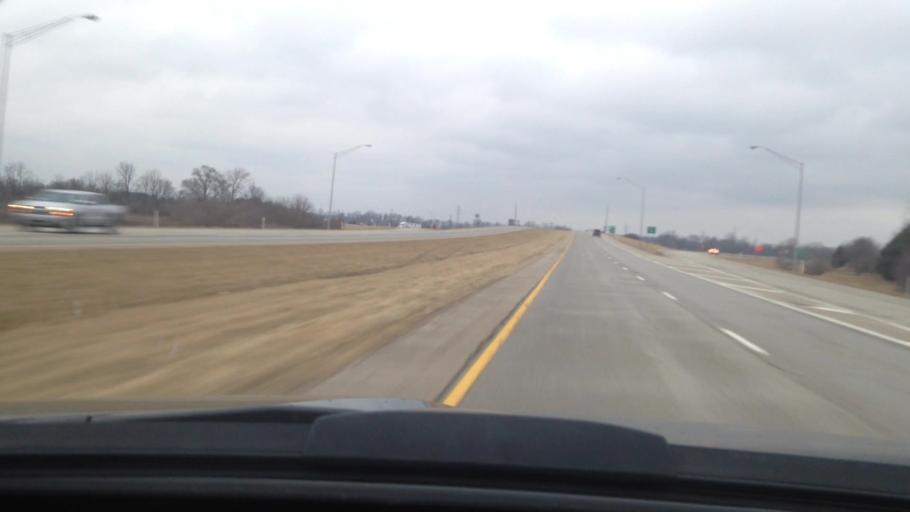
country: US
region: Indiana
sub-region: Delaware County
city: Muncie
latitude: 40.1492
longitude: -85.3624
